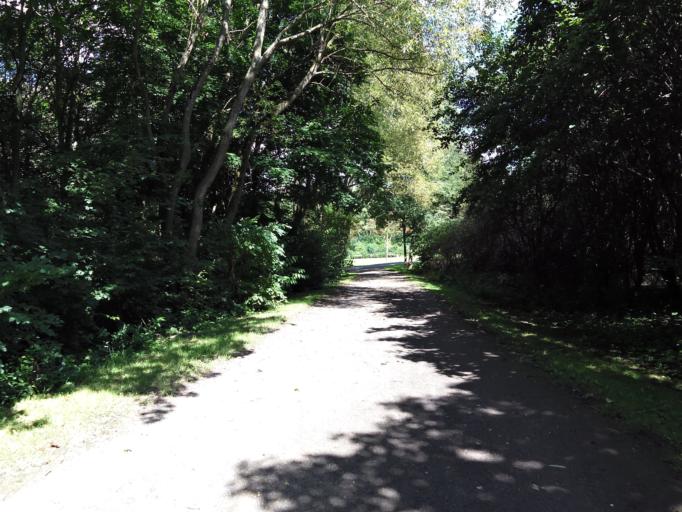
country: DE
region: Saxony
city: Markkleeberg
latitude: 51.2971
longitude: 12.4094
